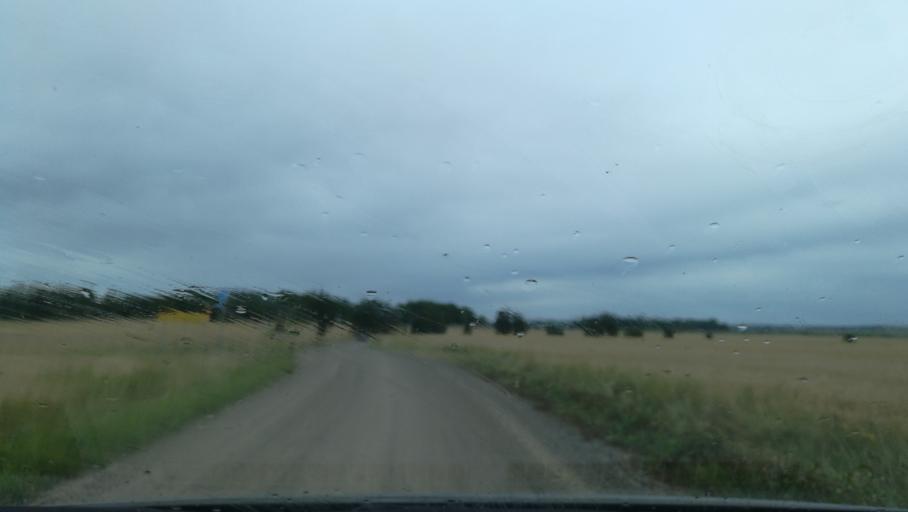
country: SE
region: Vaestmanland
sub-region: Vasteras
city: Tillberga
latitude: 59.7168
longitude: 16.6346
